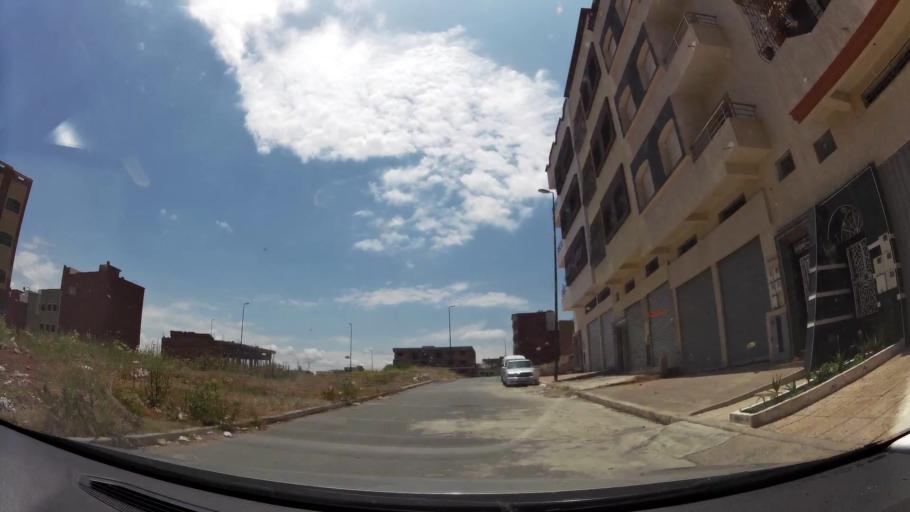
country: MA
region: Gharb-Chrarda-Beni Hssen
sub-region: Kenitra Province
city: Kenitra
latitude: 34.2718
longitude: -6.6184
